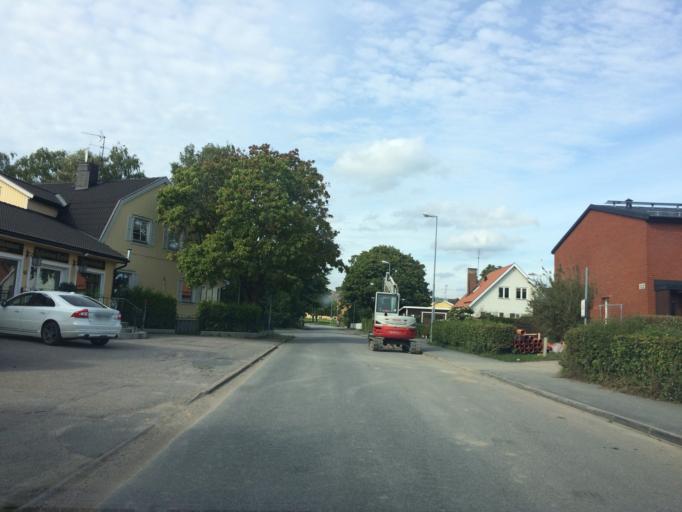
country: SE
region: Stockholm
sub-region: Sollentuna Kommun
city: Sollentuna
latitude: 59.4393
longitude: 17.9433
